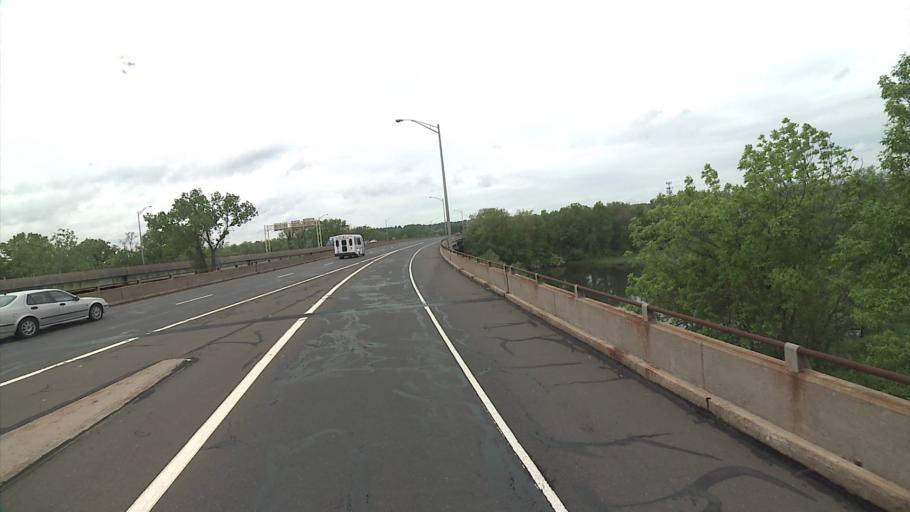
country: US
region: Connecticut
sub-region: New Haven County
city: North Haven
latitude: 41.3766
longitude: -72.8717
